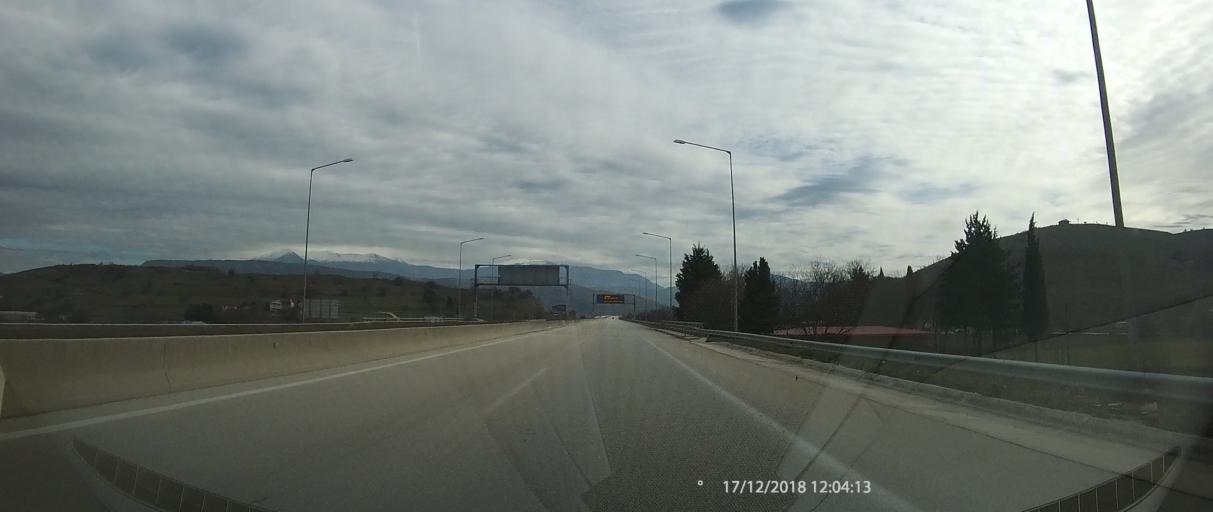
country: GR
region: Epirus
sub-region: Nomos Ioanninon
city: Katsikas
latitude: 39.6034
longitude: 20.8782
